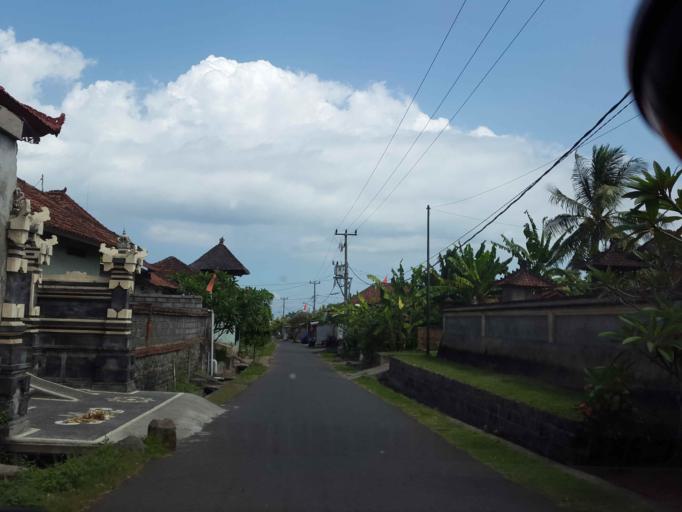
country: ID
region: Bali
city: Klungkung
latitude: -8.5510
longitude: 115.3787
